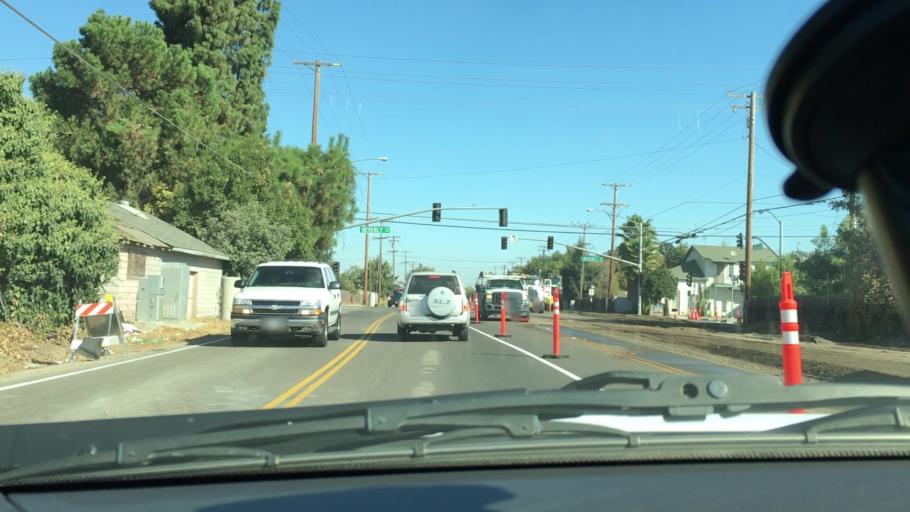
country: US
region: California
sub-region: Stanislaus County
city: West Modesto
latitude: 37.6209
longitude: -121.0305
